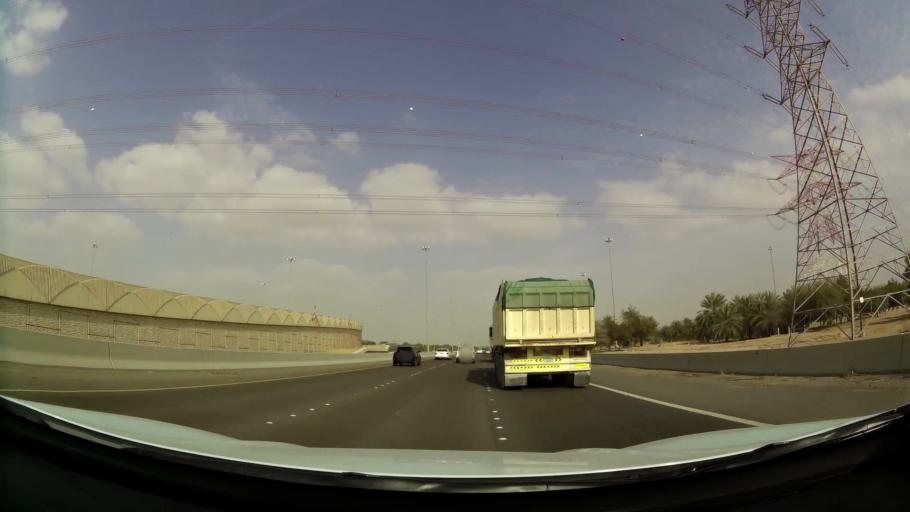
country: AE
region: Abu Dhabi
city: Abu Dhabi
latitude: 24.4210
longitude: 54.5138
